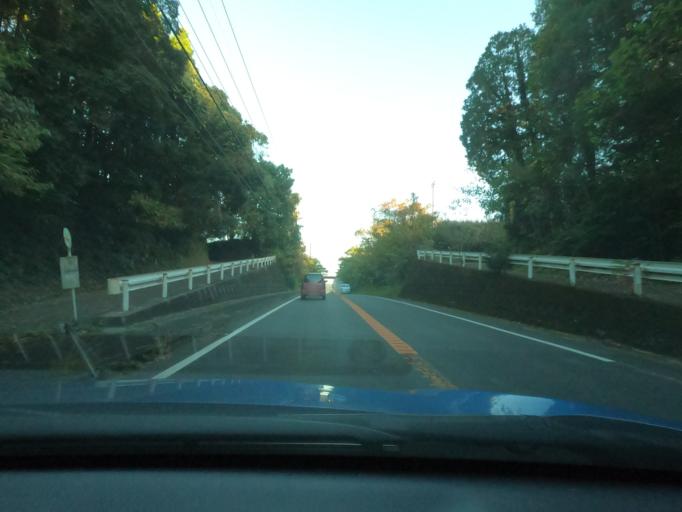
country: JP
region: Kagoshima
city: Satsumasendai
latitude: 31.8120
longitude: 130.3798
